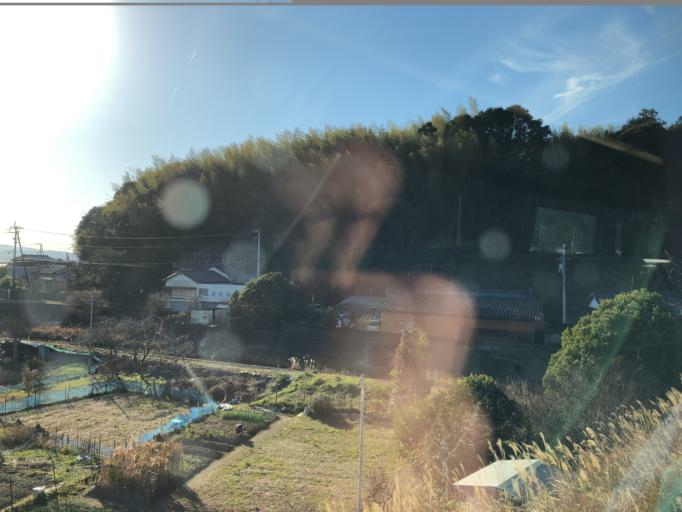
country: JP
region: Kochi
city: Nakamura
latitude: 33.0393
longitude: 133.0706
